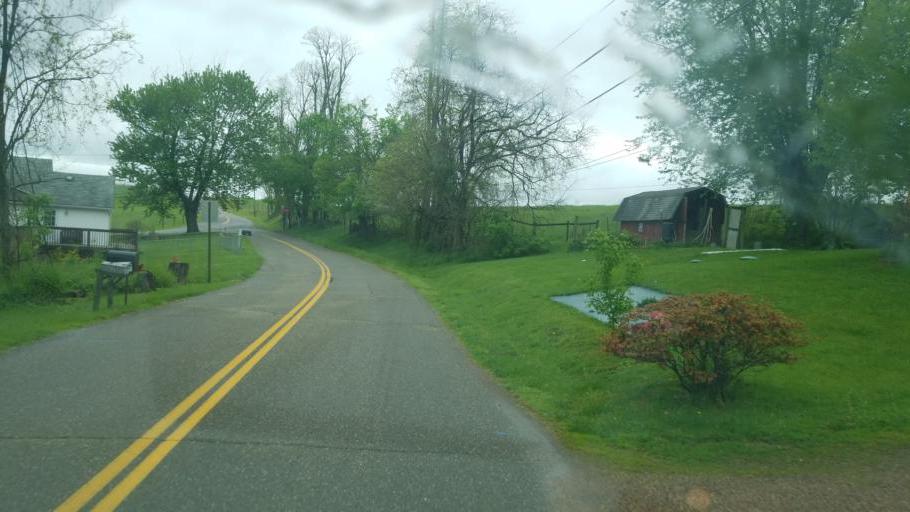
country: US
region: Ohio
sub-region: Jefferson County
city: Tiltonsville
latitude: 40.2229
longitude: -80.7172
